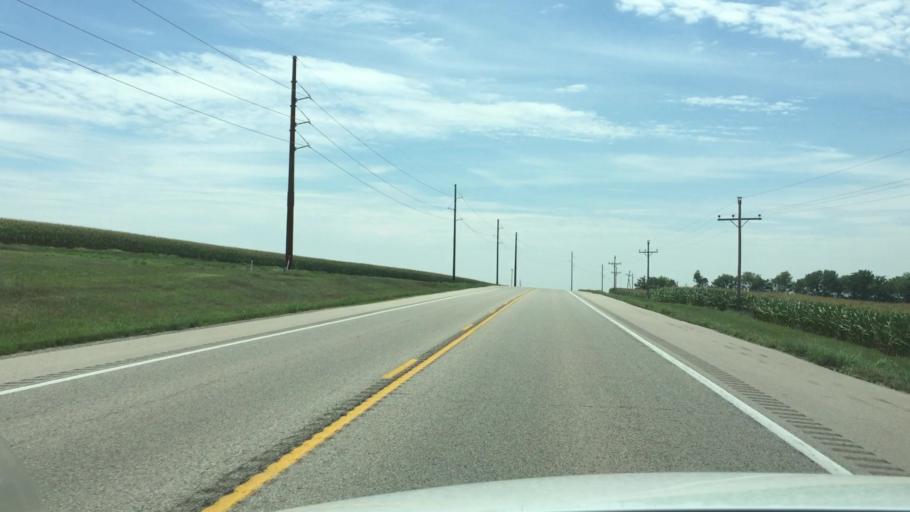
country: US
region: Kansas
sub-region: Nemaha County
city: Sabetha
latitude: 39.8230
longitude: -95.7302
